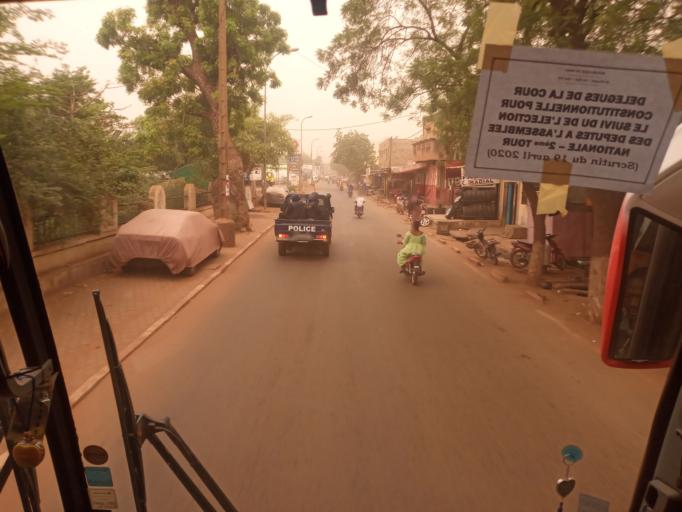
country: ML
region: Bamako
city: Bamako
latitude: 12.6520
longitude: -7.9882
